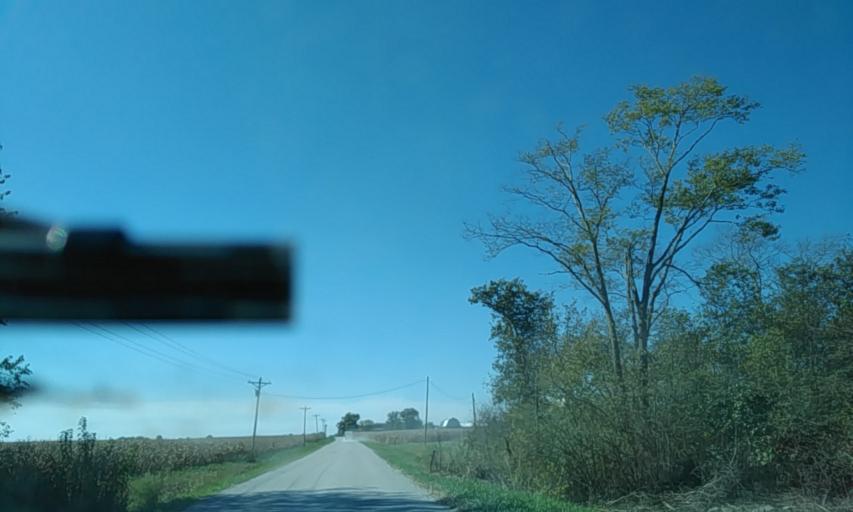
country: US
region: Illinois
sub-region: Bond County
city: Greenville
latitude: 38.9817
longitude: -89.4437
